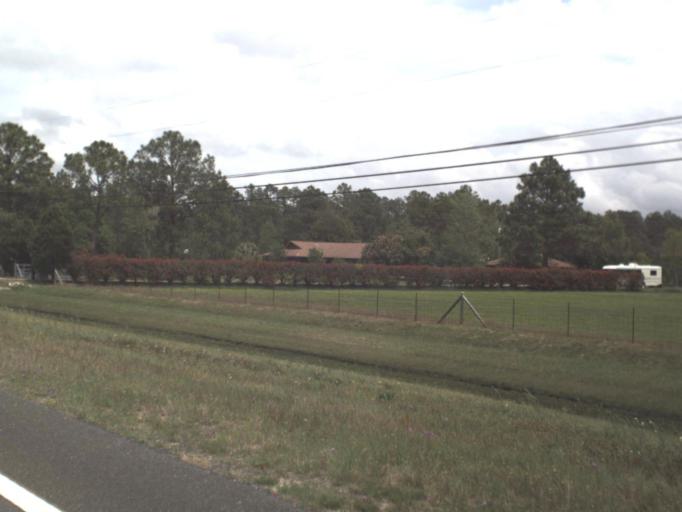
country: US
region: Florida
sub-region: Santa Rosa County
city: Bagdad
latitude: 30.5064
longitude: -87.0814
